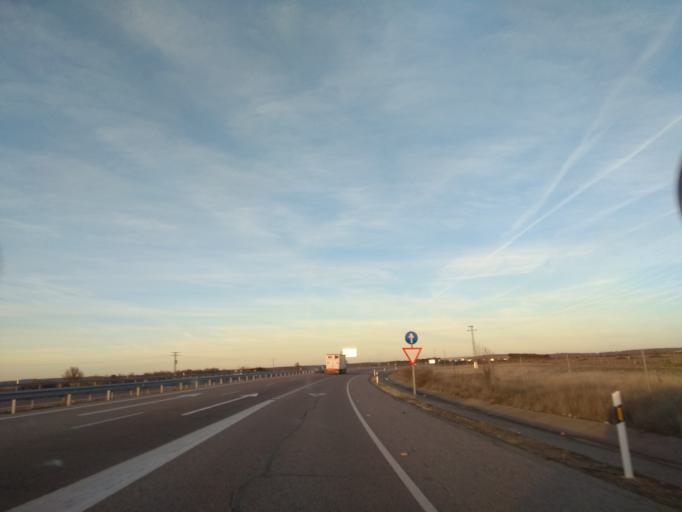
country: ES
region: Castille and Leon
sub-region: Provincia de Salamanca
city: Castraz
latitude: 40.7153
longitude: -6.3881
